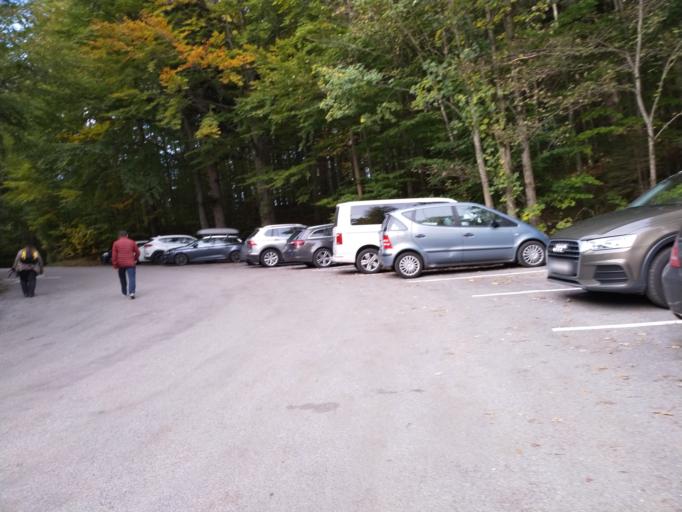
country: AT
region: Tyrol
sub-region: Politischer Bezirk Reutte
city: Vils
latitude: 47.5632
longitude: 10.6402
